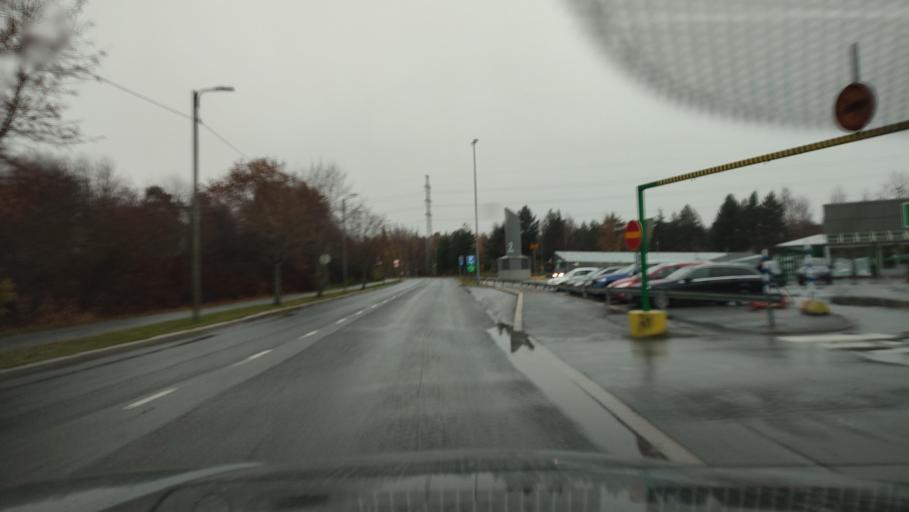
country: FI
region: Ostrobothnia
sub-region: Vaasa
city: Vaasa
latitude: 63.1027
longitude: 21.6478
